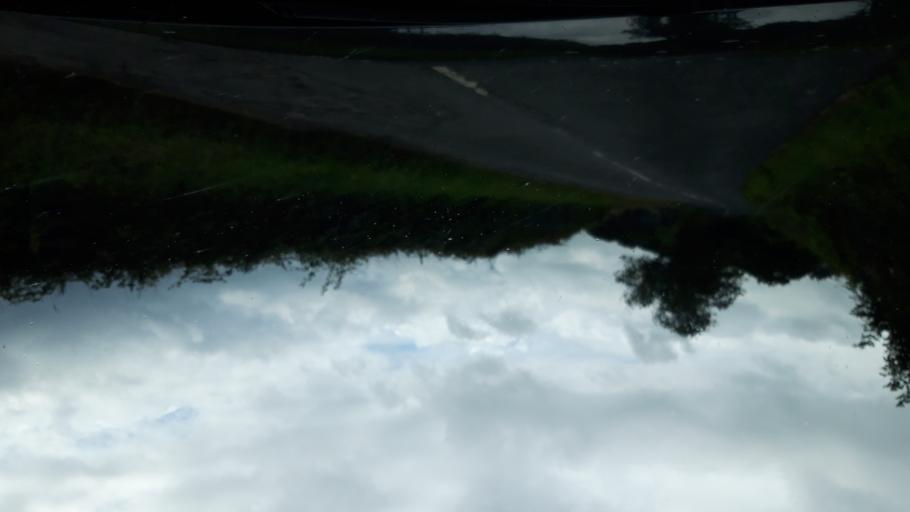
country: IE
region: Munster
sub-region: County Cork
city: Castlemartyr
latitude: 52.1357
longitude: -8.0424
